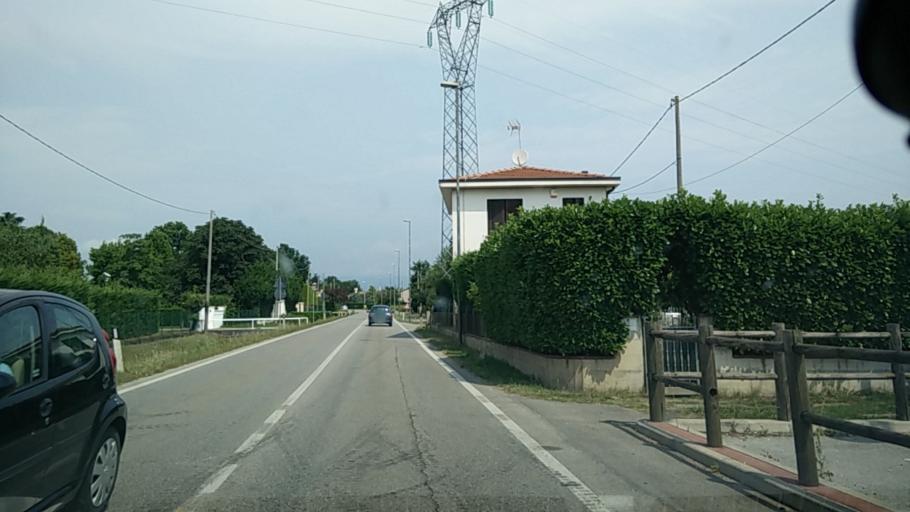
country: IT
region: Veneto
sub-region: Provincia di Treviso
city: Ponzano
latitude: 45.7294
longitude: 12.1955
